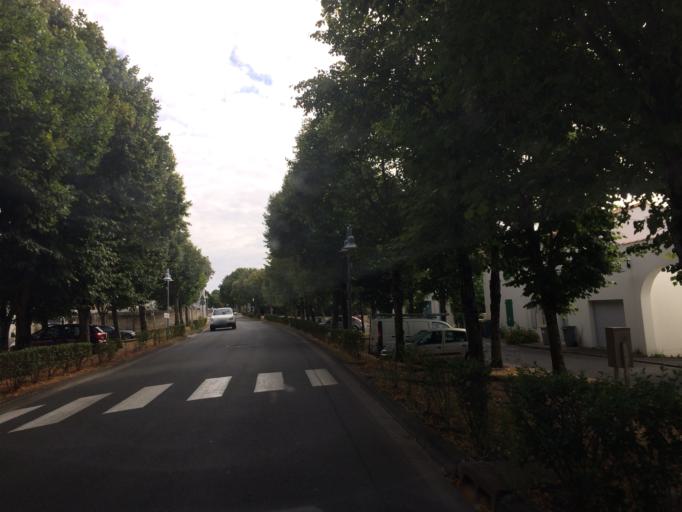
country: FR
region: Poitou-Charentes
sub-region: Departement de la Charente-Maritime
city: La Flotte
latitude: 46.1836
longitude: -1.3305
